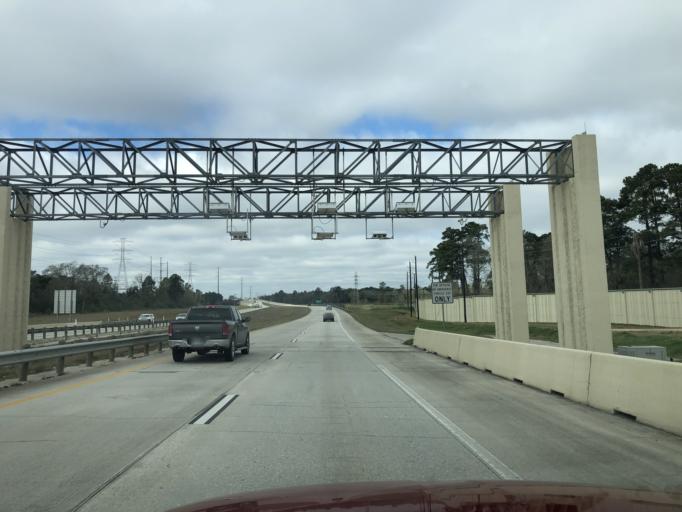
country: US
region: Texas
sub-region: Harris County
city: Spring
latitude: 30.0933
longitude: -95.4810
